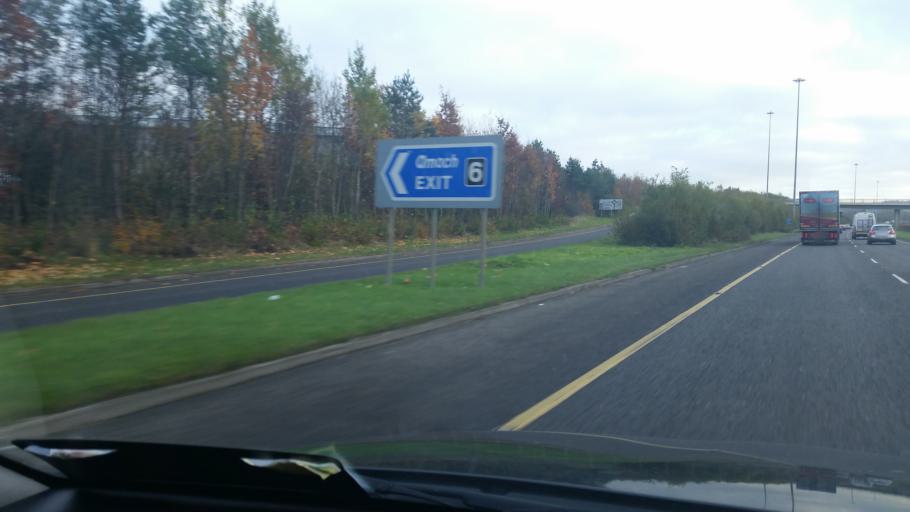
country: IE
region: Leinster
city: Balrothery
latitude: 53.6006
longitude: -6.2229
